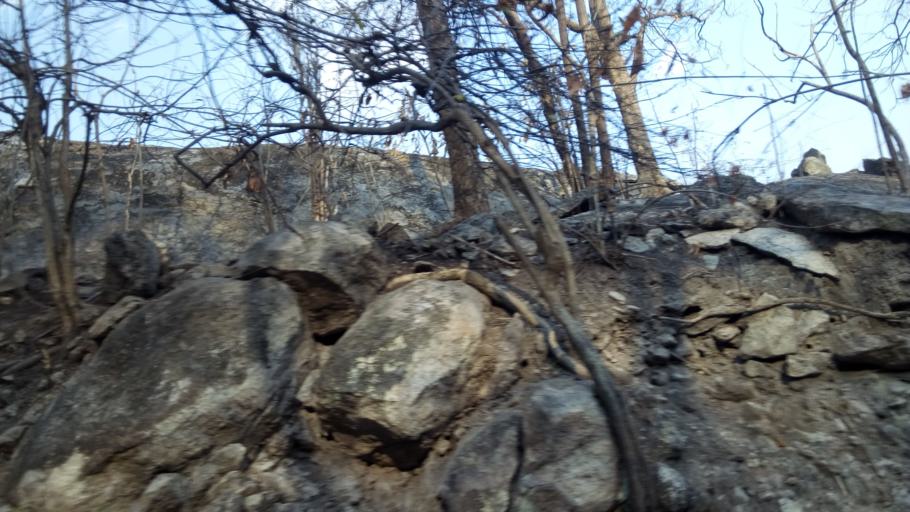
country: TH
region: Sara Buri
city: Saraburi
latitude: 14.4603
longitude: 100.9505
